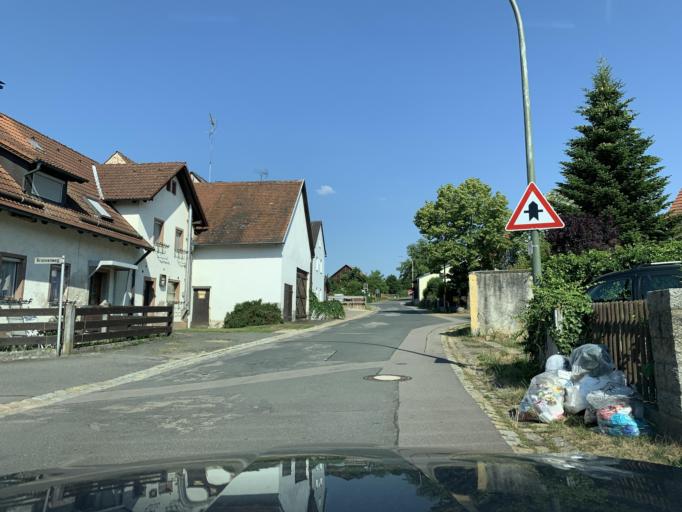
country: DE
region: Bavaria
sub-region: Upper Palatinate
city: Altendorf
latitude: 49.3976
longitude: 12.3086
